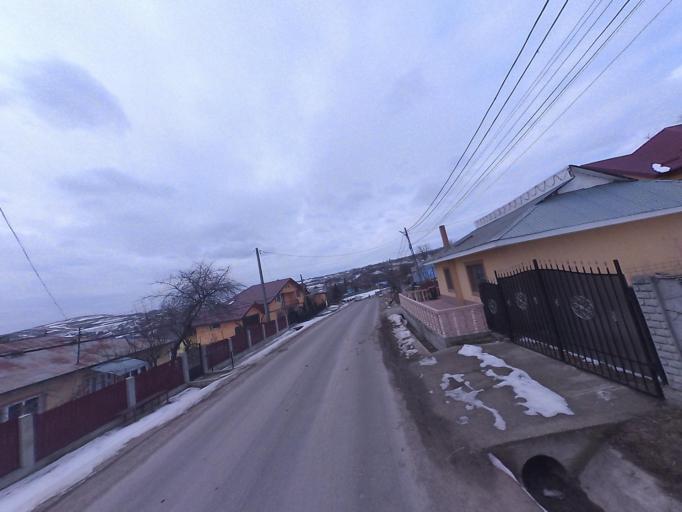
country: RO
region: Iasi
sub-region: Comuna Tibanesti
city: Glodenii Gandului
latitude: 46.9778
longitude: 27.3038
